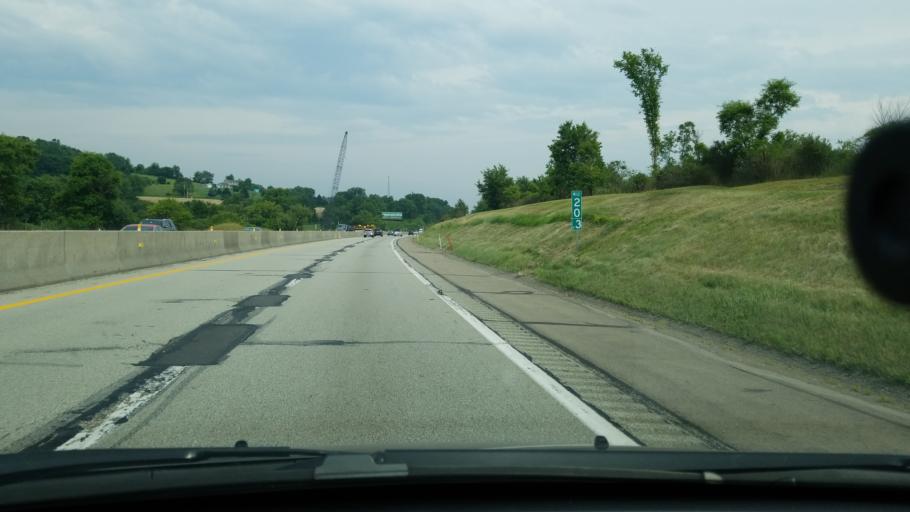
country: US
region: Pennsylvania
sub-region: Beaver County
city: Freedom
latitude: 40.7547
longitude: -80.2171
